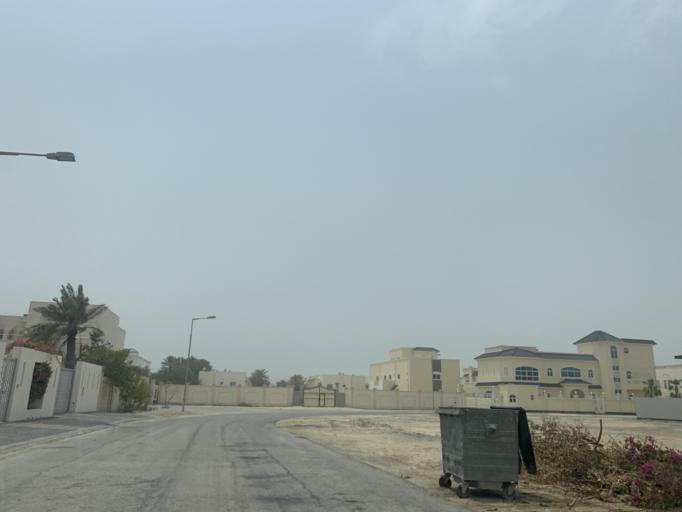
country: BH
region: Central Governorate
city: Madinat Hamad
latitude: 26.1687
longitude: 50.4732
